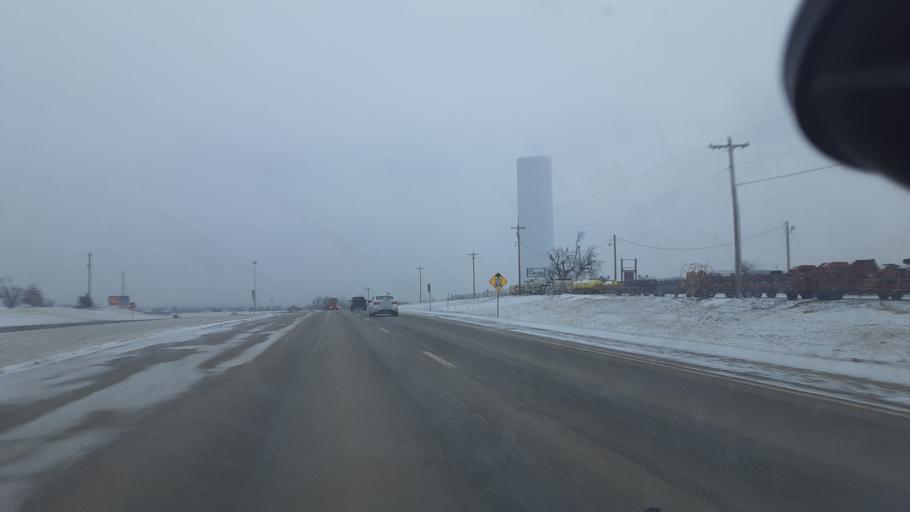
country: US
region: Oklahoma
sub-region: Logan County
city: Guthrie
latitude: 35.8851
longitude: -97.3789
